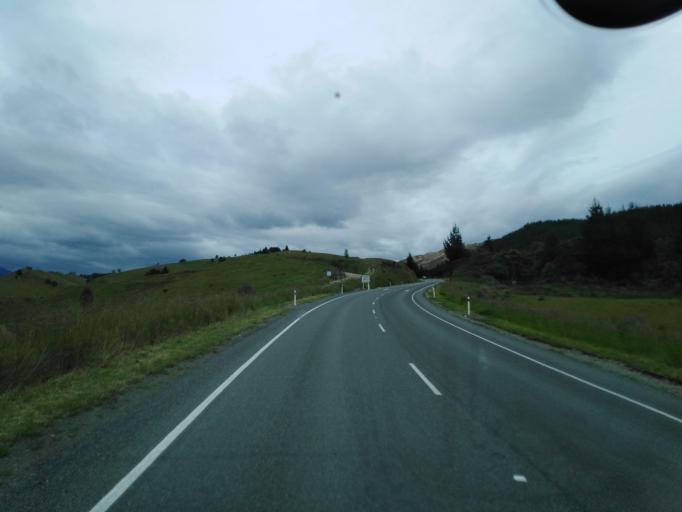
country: NZ
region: Tasman
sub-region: Tasman District
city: Wakefield
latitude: -41.4617
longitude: 172.9514
